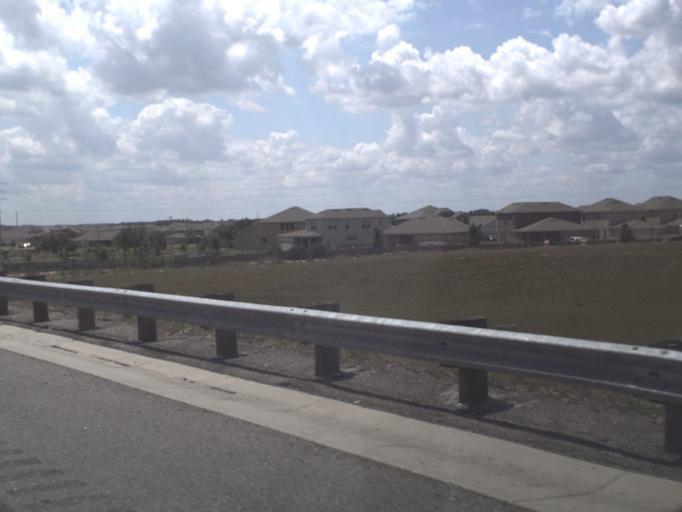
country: US
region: Florida
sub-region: Polk County
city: Citrus Ridge
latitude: 28.4390
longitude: -81.6394
